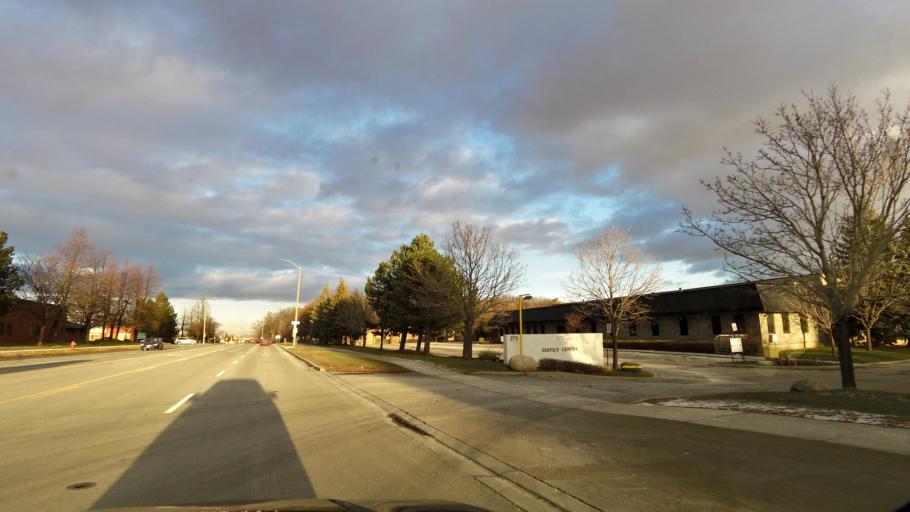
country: CA
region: Ontario
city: Mississauga
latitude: 43.6237
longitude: -79.6591
